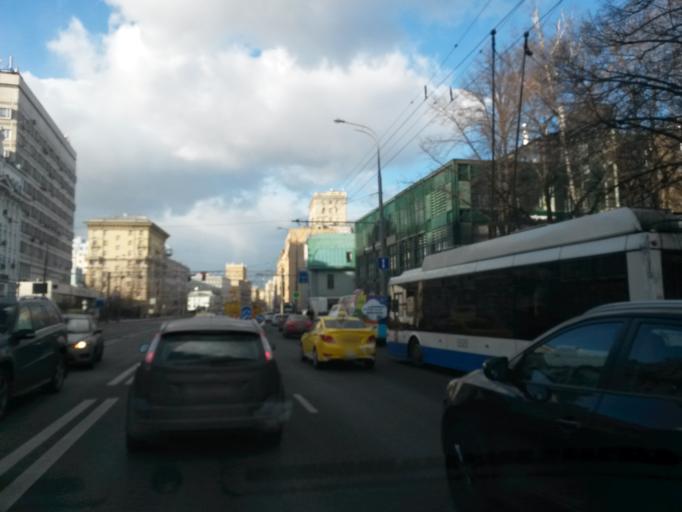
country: RU
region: Moscow
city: Mar'ina Roshcha
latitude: 55.7775
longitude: 37.6326
